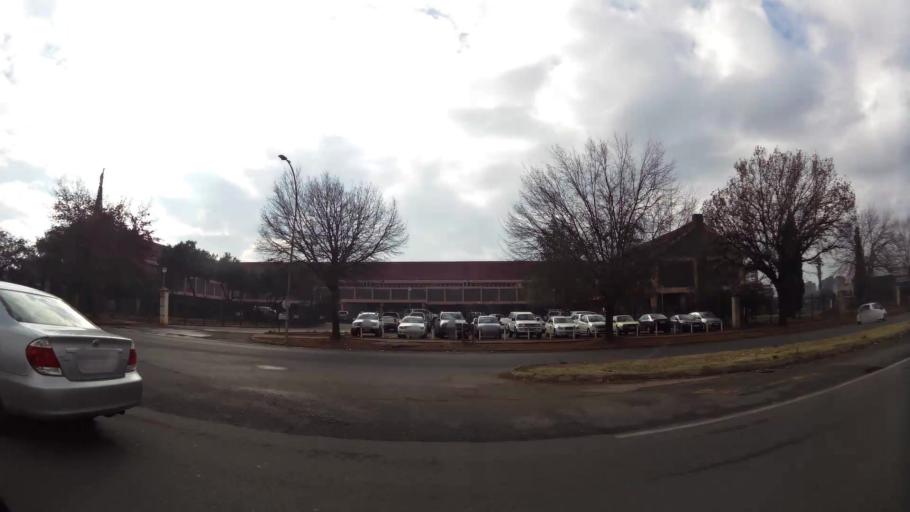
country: ZA
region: Gauteng
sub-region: Sedibeng District Municipality
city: Vanderbijlpark
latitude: -26.7006
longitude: 27.8329
